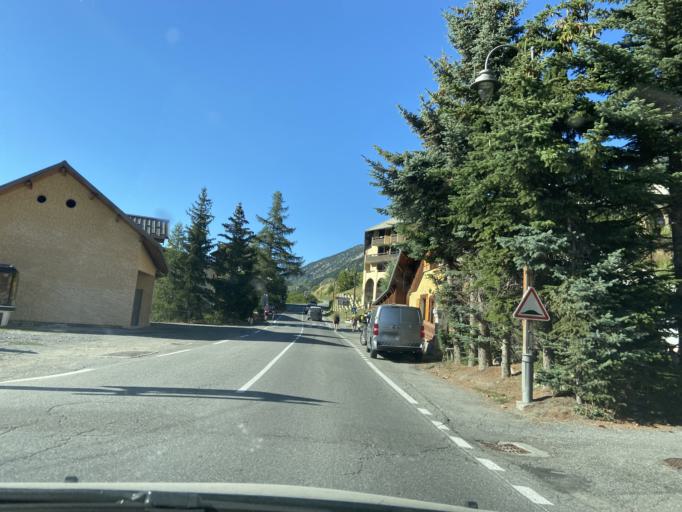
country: FR
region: Provence-Alpes-Cote d'Azur
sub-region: Departement des Hautes-Alpes
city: Guillestre
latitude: 44.5949
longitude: 6.6899
